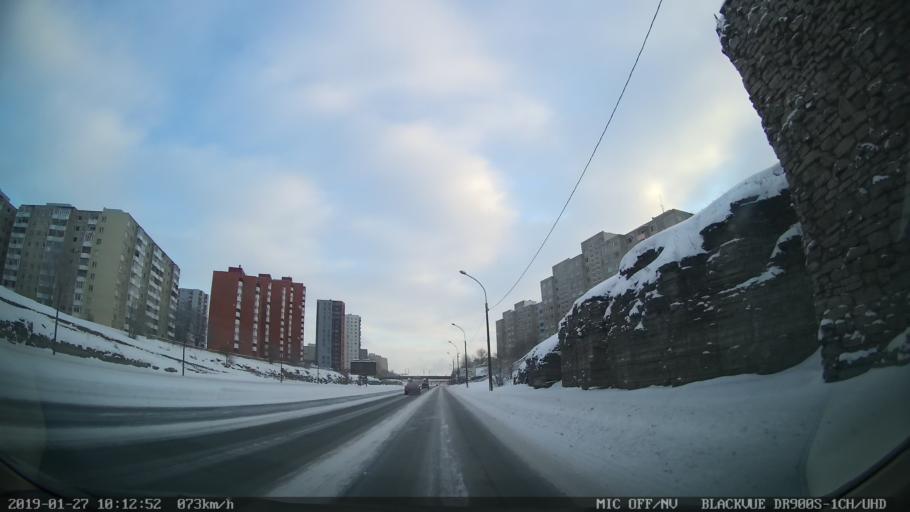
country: EE
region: Harju
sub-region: Tallinna linn
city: Kose
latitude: 59.4398
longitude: 24.8385
